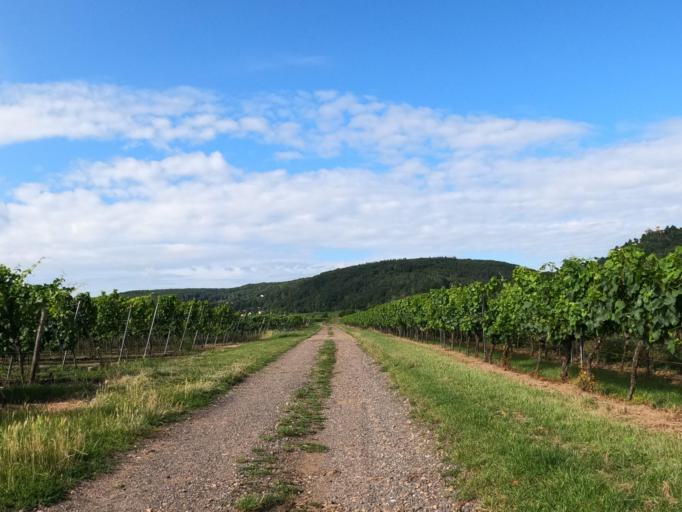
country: DE
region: Rheinland-Pfalz
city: Kleinkarlbach
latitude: 49.5331
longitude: 8.1564
